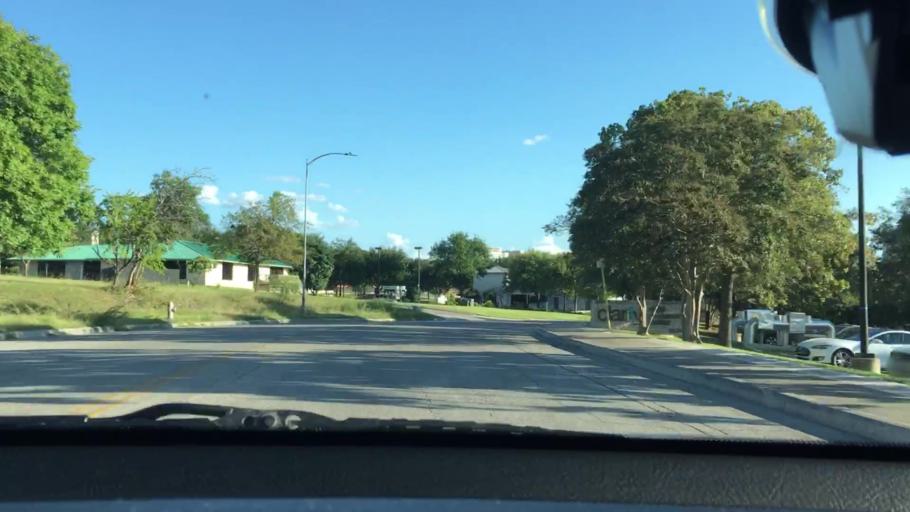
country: US
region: Texas
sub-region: Bexar County
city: Balcones Heights
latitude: 29.5202
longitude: -98.5752
